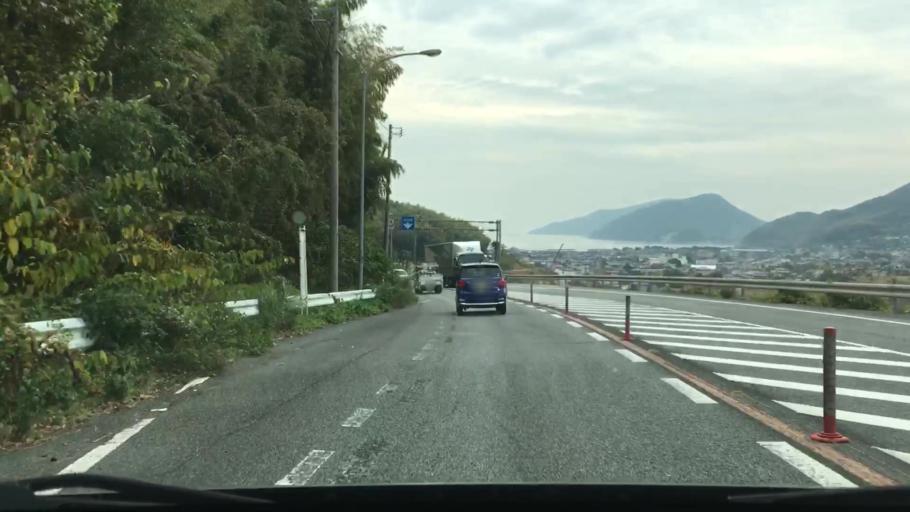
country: JP
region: Yamaguchi
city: Hofu
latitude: 34.0591
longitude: 131.6576
